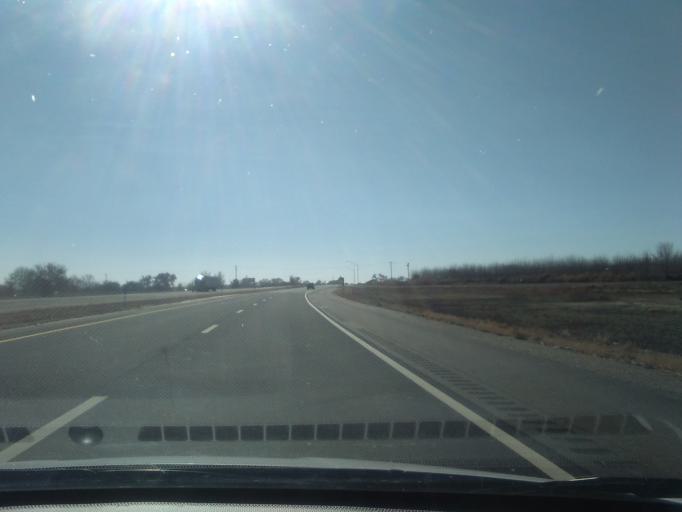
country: US
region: New Mexico
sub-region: Valencia County
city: Jarales
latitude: 34.6292
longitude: -106.7829
